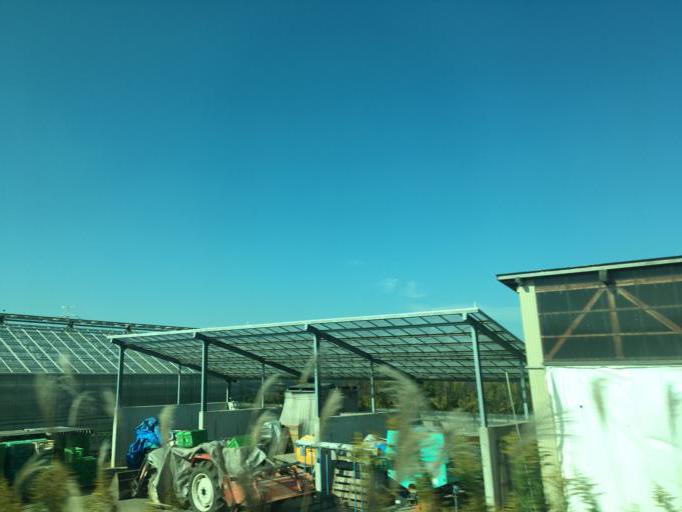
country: JP
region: Ibaraki
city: Shimodate
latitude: 36.3139
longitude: 140.0124
